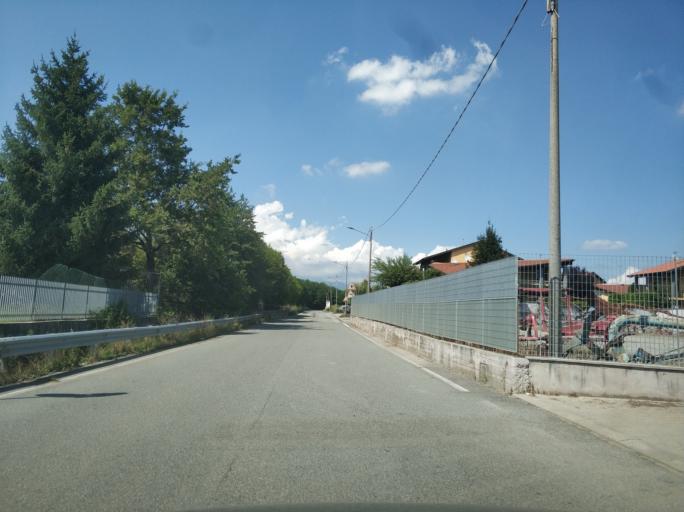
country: IT
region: Piedmont
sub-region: Provincia di Torino
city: Feletto
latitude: 45.2956
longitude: 7.7215
